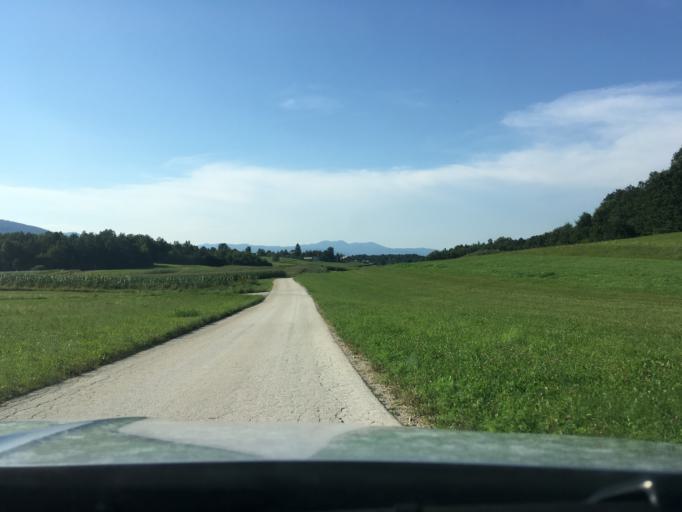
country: SI
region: Crnomelj
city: Crnomelj
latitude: 45.4639
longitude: 15.2124
